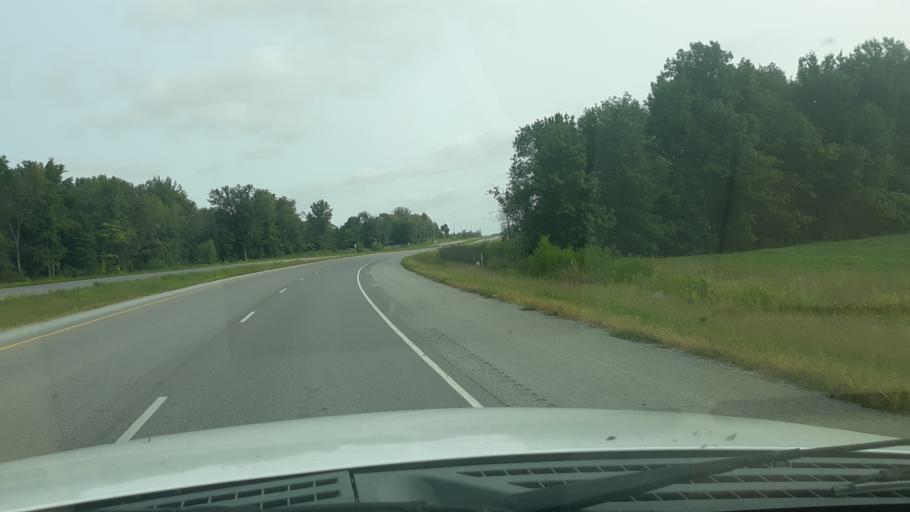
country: US
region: Illinois
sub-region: Saline County
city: Eldorado
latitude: 37.8228
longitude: -88.4268
